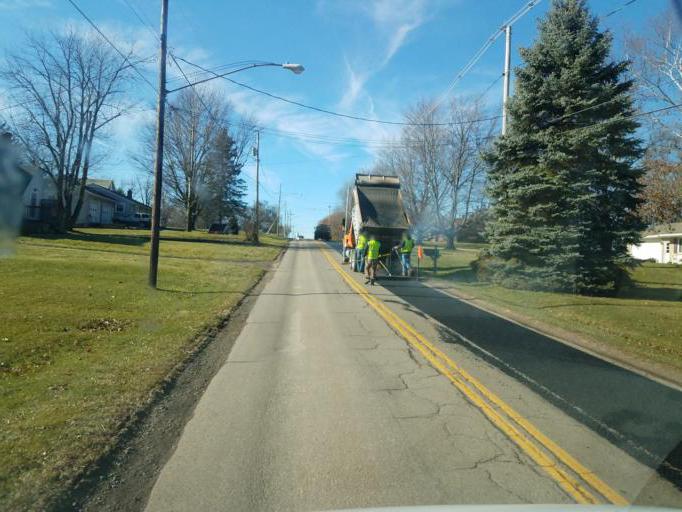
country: US
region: Ohio
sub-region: Wayne County
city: Dalton
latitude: 40.7412
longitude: -81.7525
